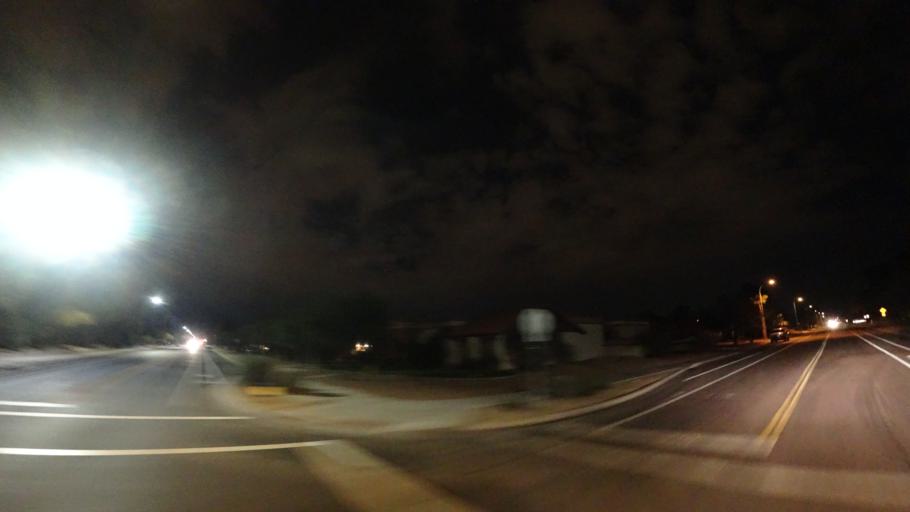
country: US
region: Arizona
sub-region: Maricopa County
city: San Carlos
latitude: 33.3278
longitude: -111.8504
